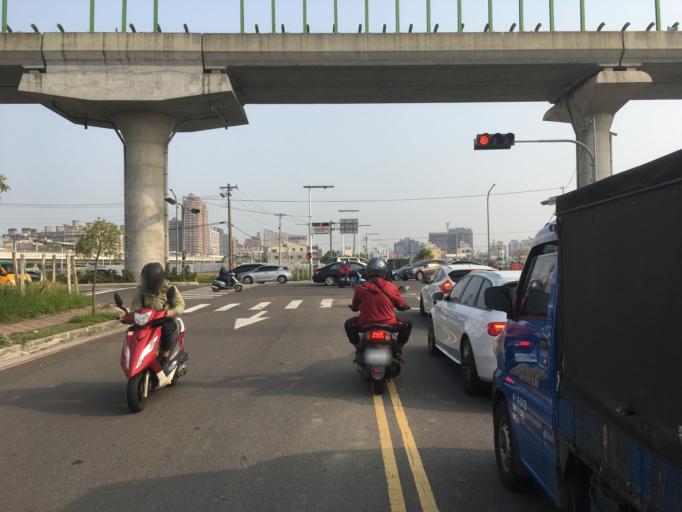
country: TW
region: Taiwan
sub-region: Taichung City
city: Taichung
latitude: 24.1818
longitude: 120.7039
